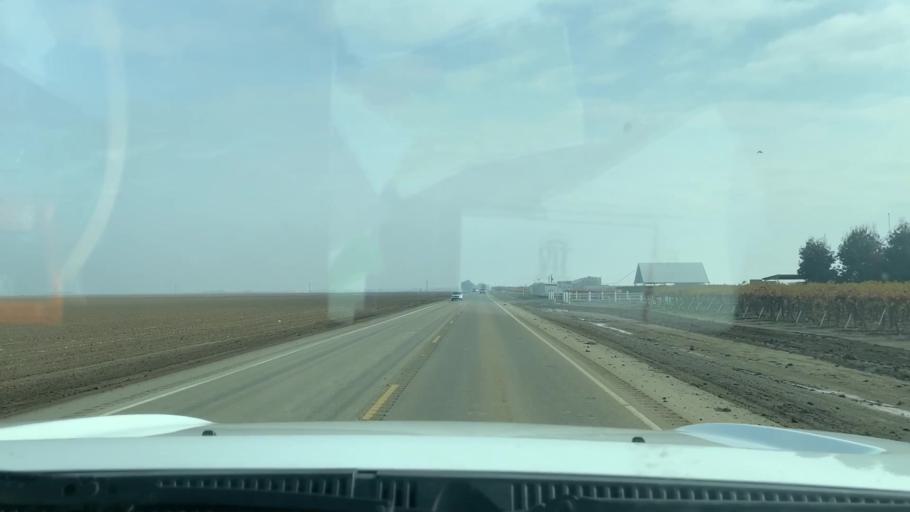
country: US
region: California
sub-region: Kings County
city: Lemoore Station
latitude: 36.2555
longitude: -119.9583
